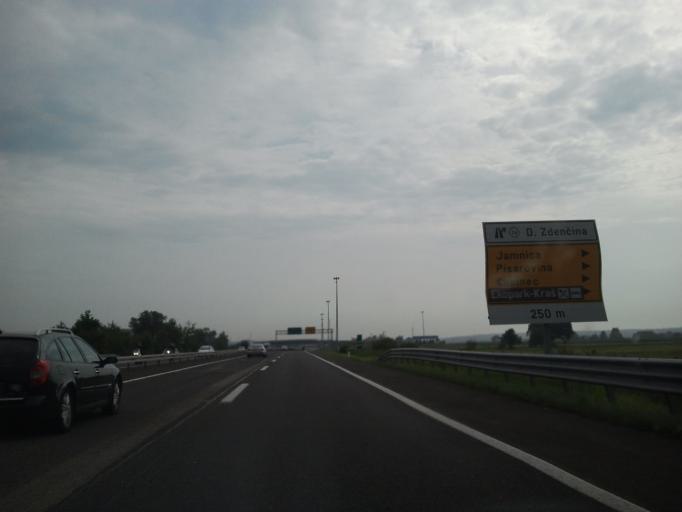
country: HR
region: Grad Zagreb
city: Horvati
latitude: 45.6741
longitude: 15.7472
